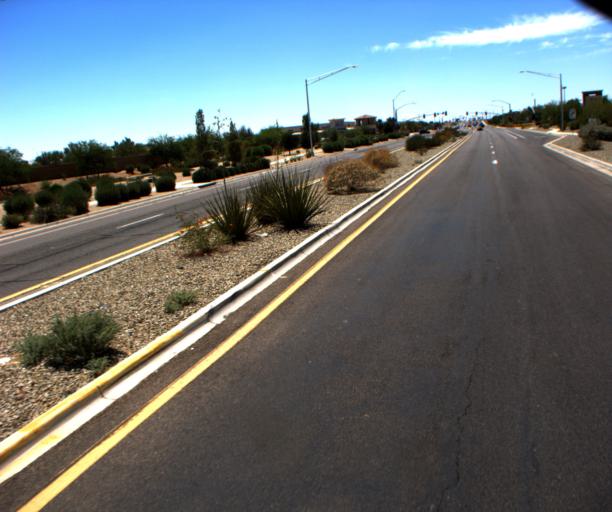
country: US
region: Arizona
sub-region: Pinal County
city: Casa Grande
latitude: 32.8797
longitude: -111.6769
